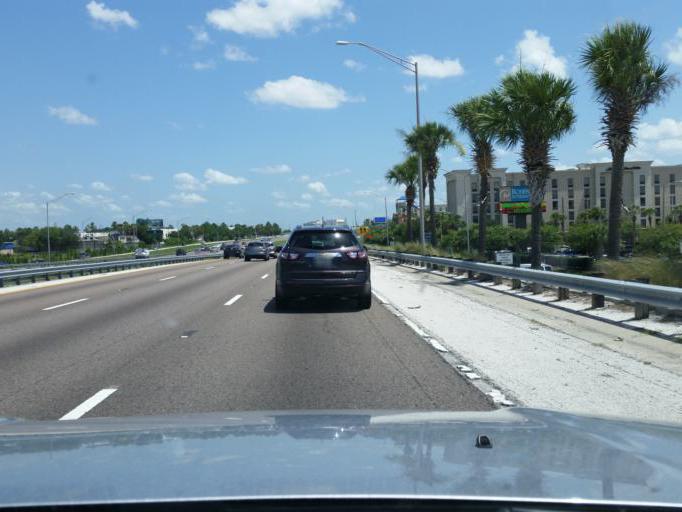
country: US
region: Florida
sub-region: Orange County
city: Doctor Phillips
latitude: 28.4515
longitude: -81.4741
